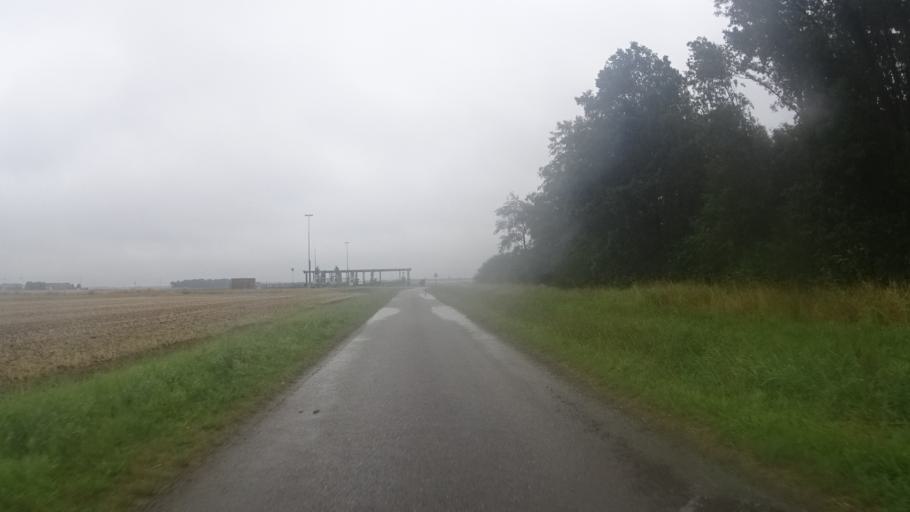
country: NL
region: Groningen
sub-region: Gemeente Veendam
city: Veendam
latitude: 53.1793
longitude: 6.8775
